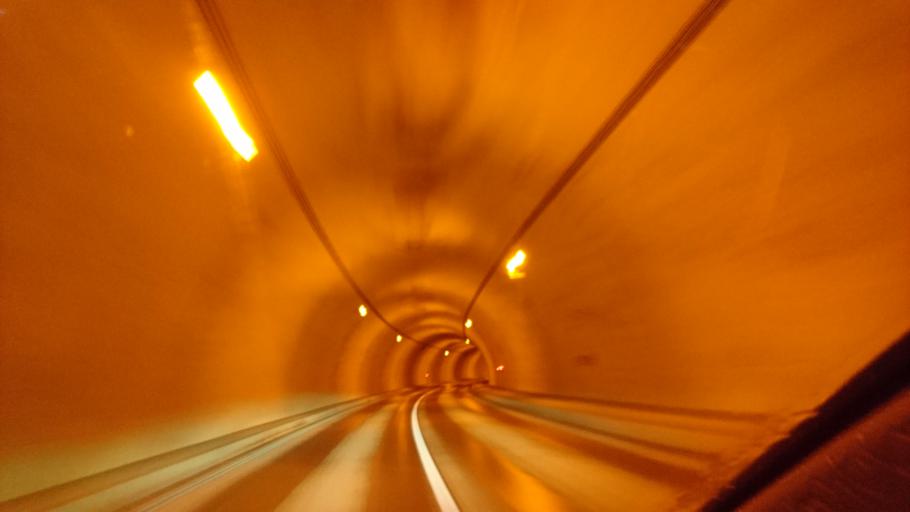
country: JP
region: Iwate
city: Mizusawa
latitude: 39.1265
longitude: 140.9295
